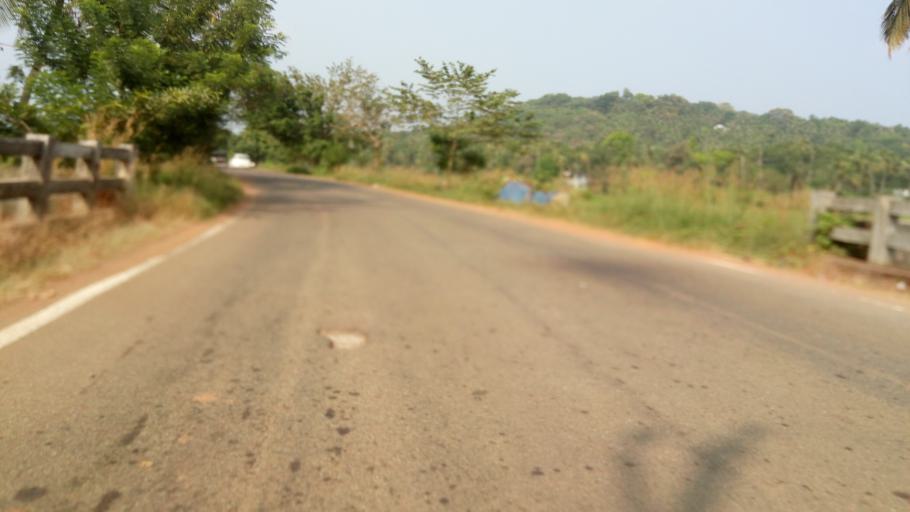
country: IN
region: Kerala
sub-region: Malappuram
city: Malappuram
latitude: 10.9987
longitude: 76.0149
